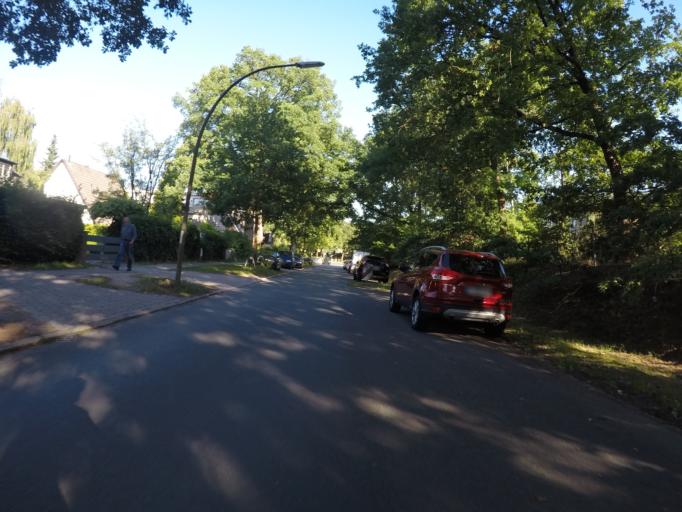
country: DE
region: Hamburg
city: Langenhorn
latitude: 53.6748
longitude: 10.0140
